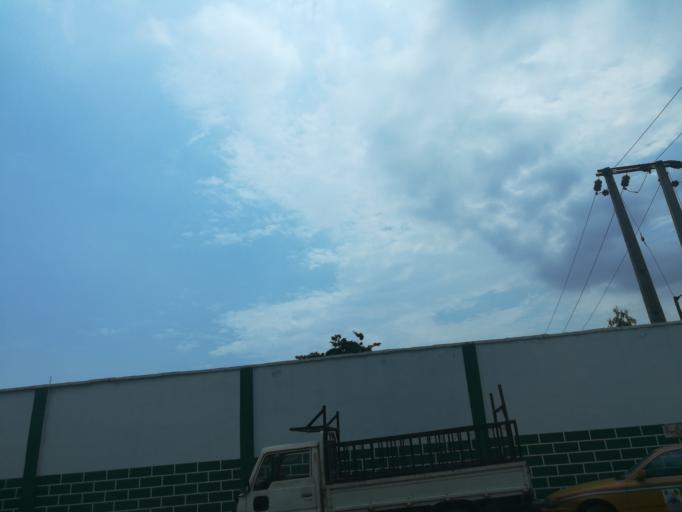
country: NG
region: Lagos
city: Ikeja
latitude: 6.6082
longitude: 3.3625
